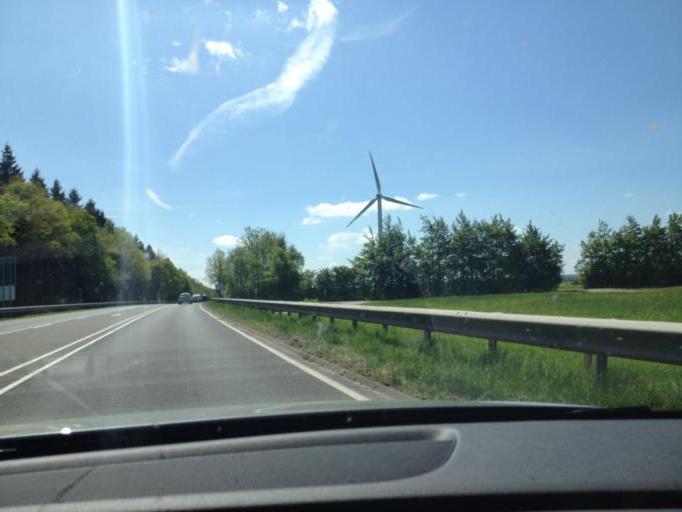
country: DE
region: North Rhine-Westphalia
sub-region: Regierungsbezirk Koln
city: Blankenheim
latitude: 50.4273
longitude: 6.6040
